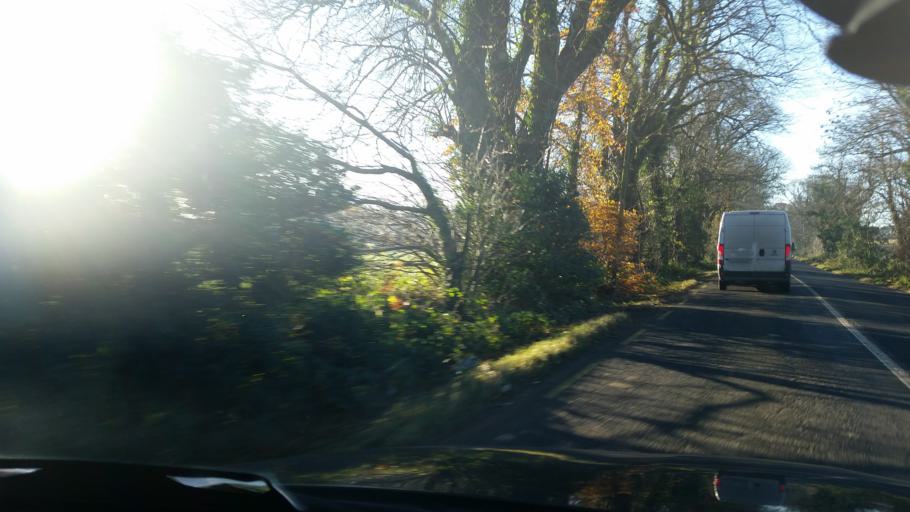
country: IE
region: Leinster
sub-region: Loch Garman
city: Ballinroad
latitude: 52.5315
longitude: -6.3517
